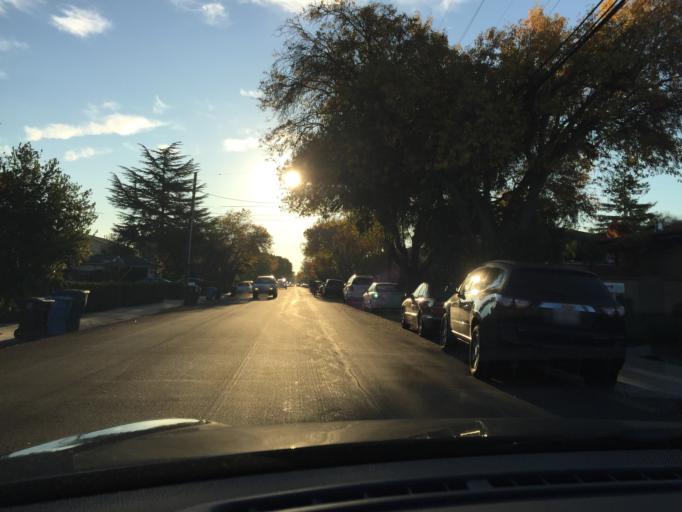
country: US
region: California
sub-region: Santa Clara County
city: Palo Alto
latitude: 37.4322
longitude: -122.1213
